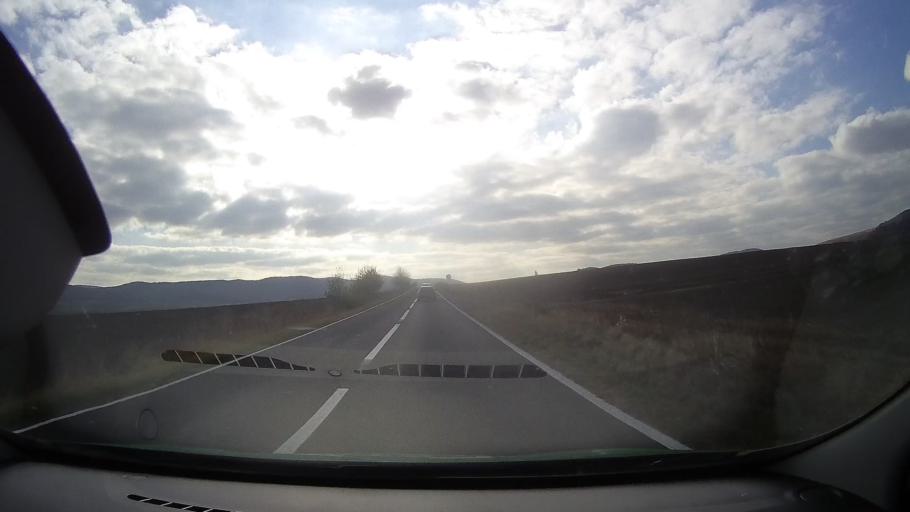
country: RO
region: Tulcea
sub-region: Comuna Nalbant
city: Nicolae Balcescu
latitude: 44.9822
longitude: 28.5509
